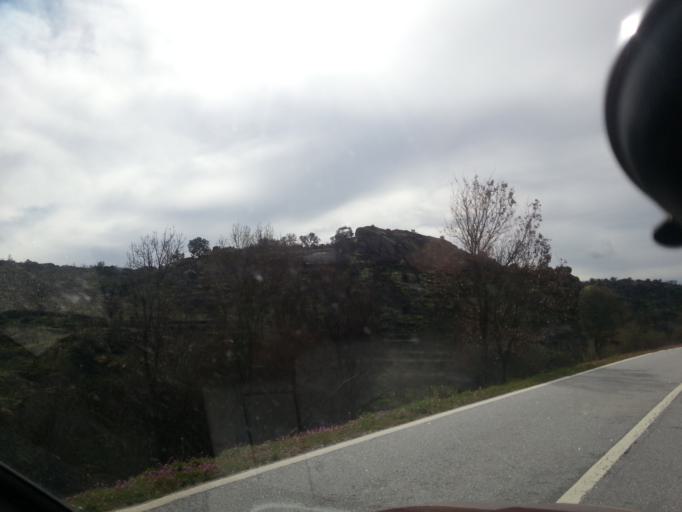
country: PT
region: Guarda
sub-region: Fornos de Algodres
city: Fornos de Algodres
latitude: 40.5661
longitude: -7.5568
